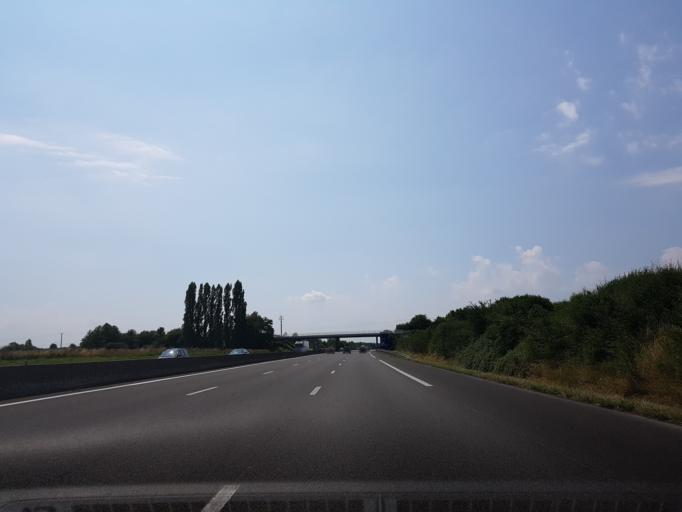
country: FR
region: Ile-de-France
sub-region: Departement des Yvelines
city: Saint-Arnoult-en-Yvelines
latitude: 48.5252
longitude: 1.9074
